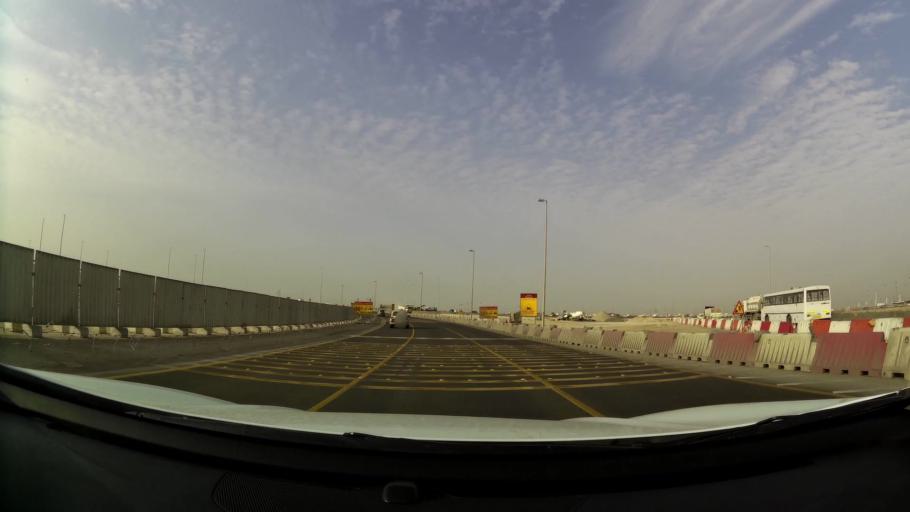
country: AE
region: Abu Dhabi
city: Abu Dhabi
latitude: 24.2879
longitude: 54.5608
